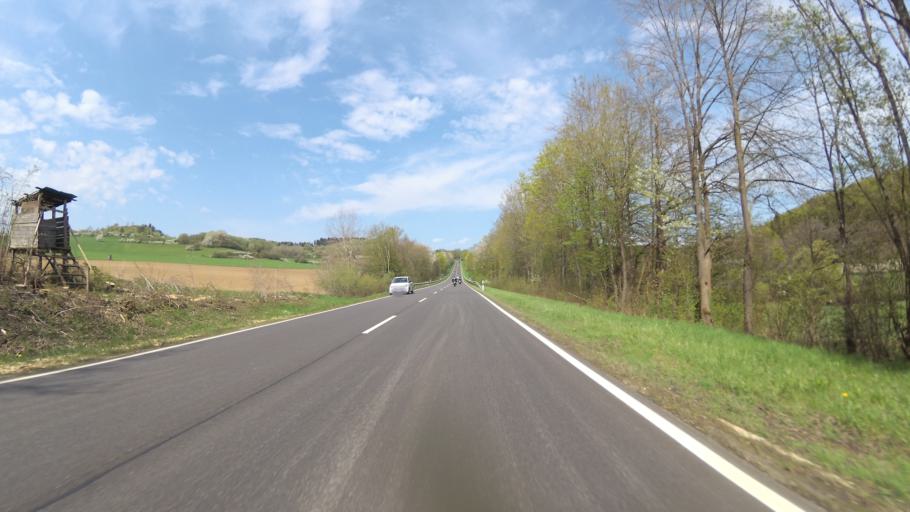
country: DE
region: Rheinland-Pfalz
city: Schonbach
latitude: 50.2208
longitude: 6.9552
